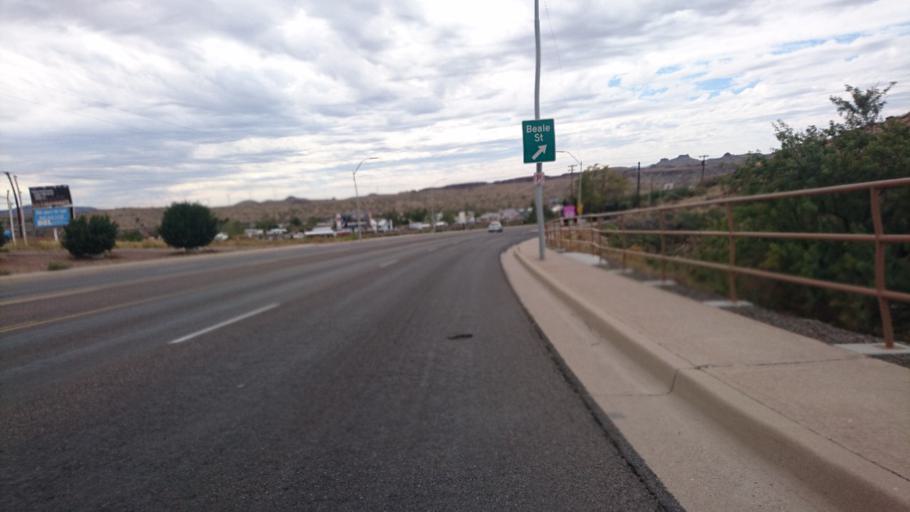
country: US
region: Arizona
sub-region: Mohave County
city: Kingman
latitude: 35.1874
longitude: -114.0390
